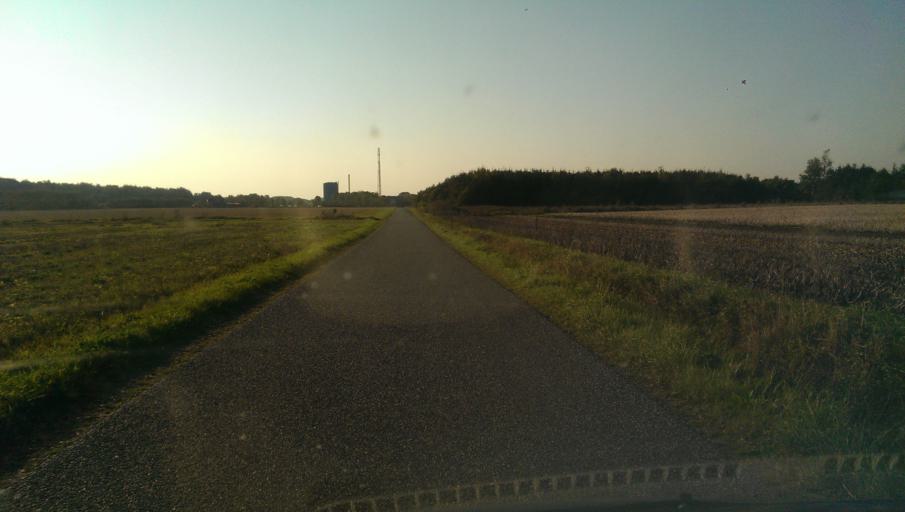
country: DK
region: South Denmark
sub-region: Esbjerg Kommune
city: Bramming
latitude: 55.4758
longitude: 8.8114
